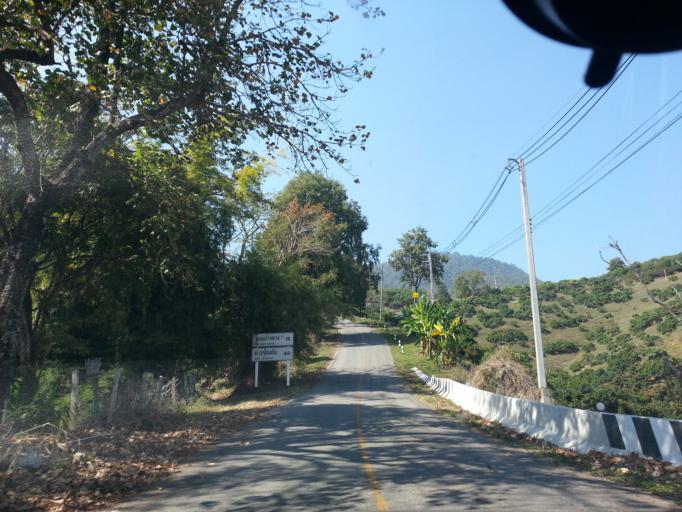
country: TH
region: Chiang Mai
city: Chai Prakan
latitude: 19.8323
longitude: 99.0998
